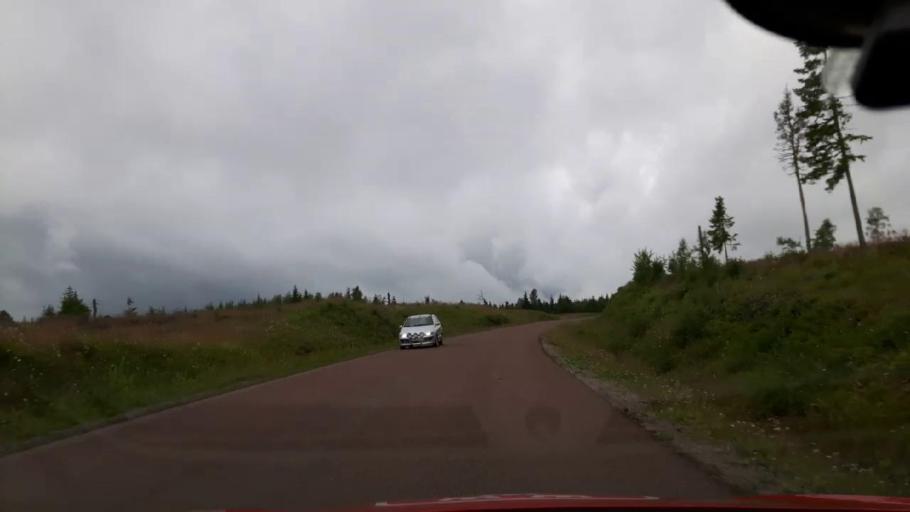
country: SE
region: Jaemtland
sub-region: Krokoms Kommun
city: Valla
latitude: 63.3726
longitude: 13.7564
